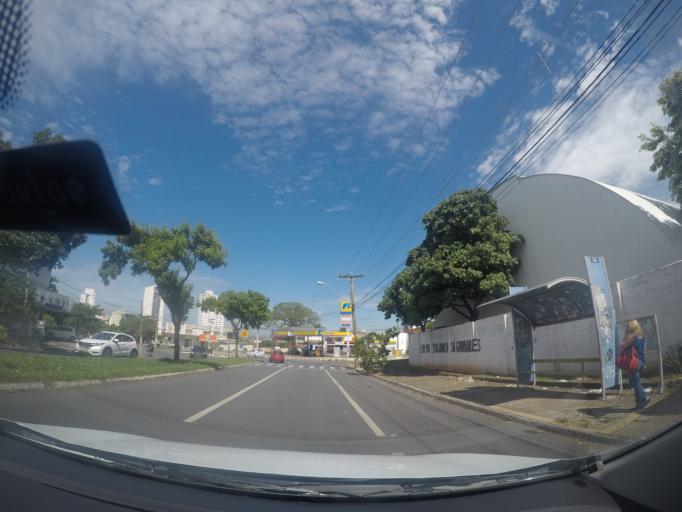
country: BR
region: Goias
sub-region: Goiania
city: Goiania
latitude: -16.7232
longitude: -49.2691
